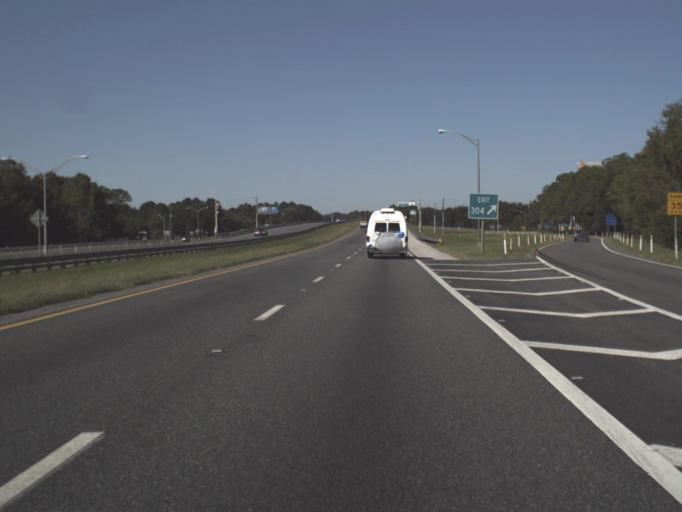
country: US
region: Florida
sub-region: Sumter County
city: Wildwood
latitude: 28.8352
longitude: -82.0419
